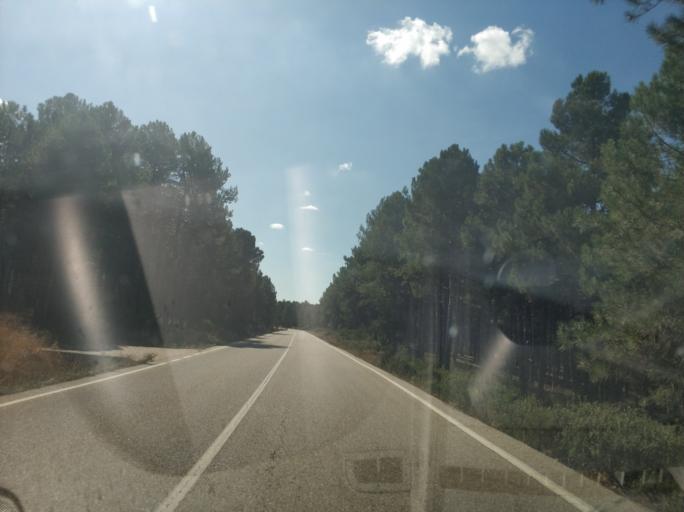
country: ES
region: Castille and Leon
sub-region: Provincia de Soria
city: Ucero
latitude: 41.7454
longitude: -3.0439
